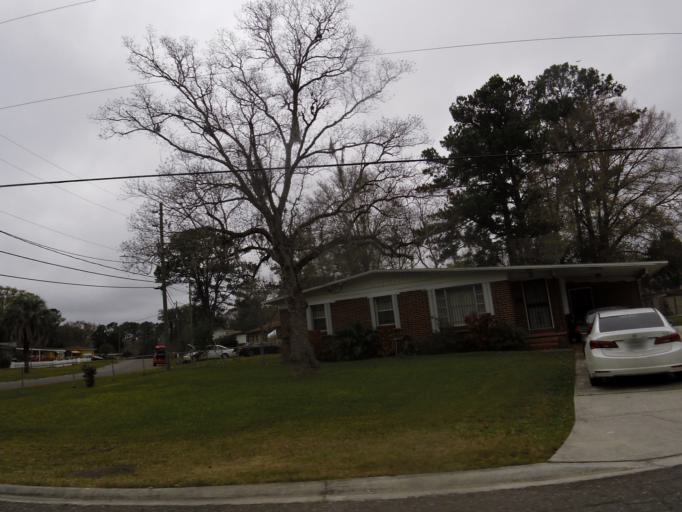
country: US
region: Florida
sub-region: Duval County
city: Jacksonville
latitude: 30.3779
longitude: -81.7177
